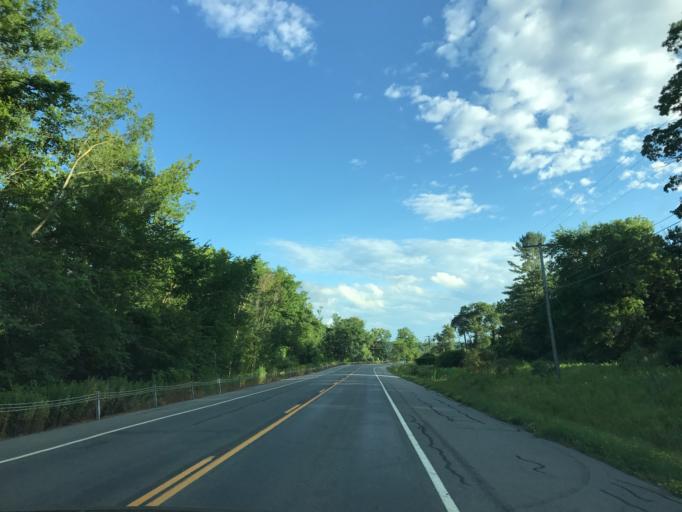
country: US
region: New York
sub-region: Saratoga County
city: Schuylerville
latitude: 43.1325
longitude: -73.5850
